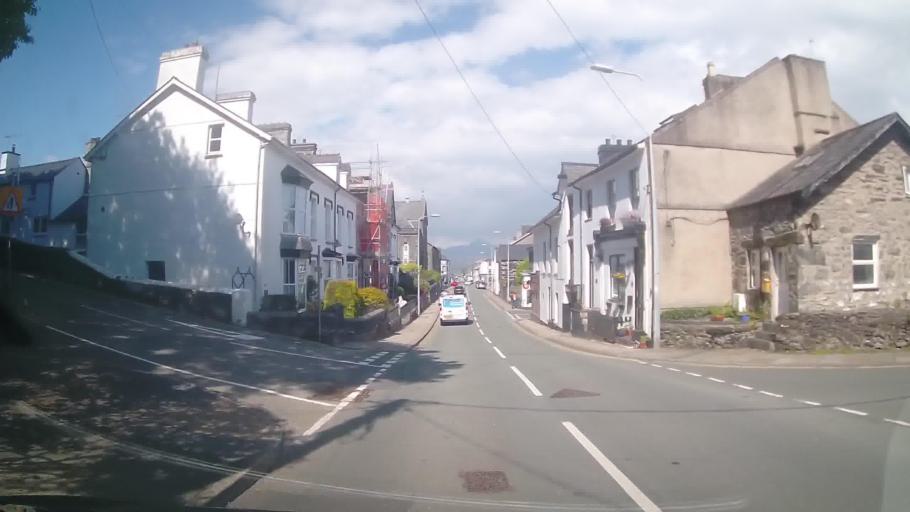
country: GB
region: Wales
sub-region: Gwynedd
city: Porthmadog
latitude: 52.9253
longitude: -4.1329
